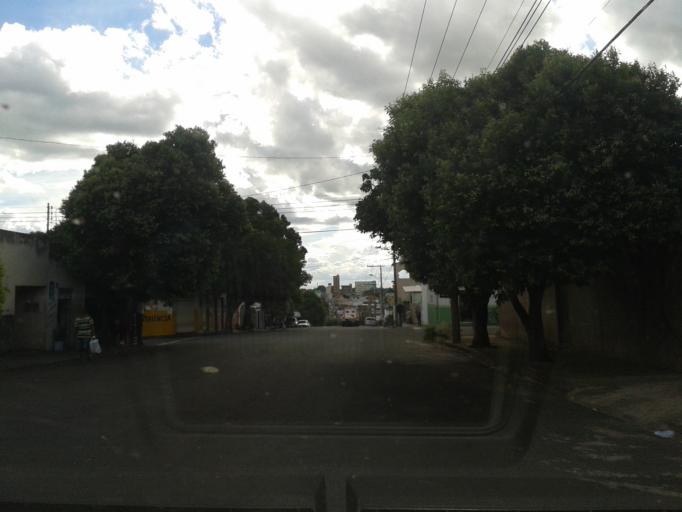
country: BR
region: Minas Gerais
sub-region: Ituiutaba
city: Ituiutaba
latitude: -18.9690
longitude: -49.4531
